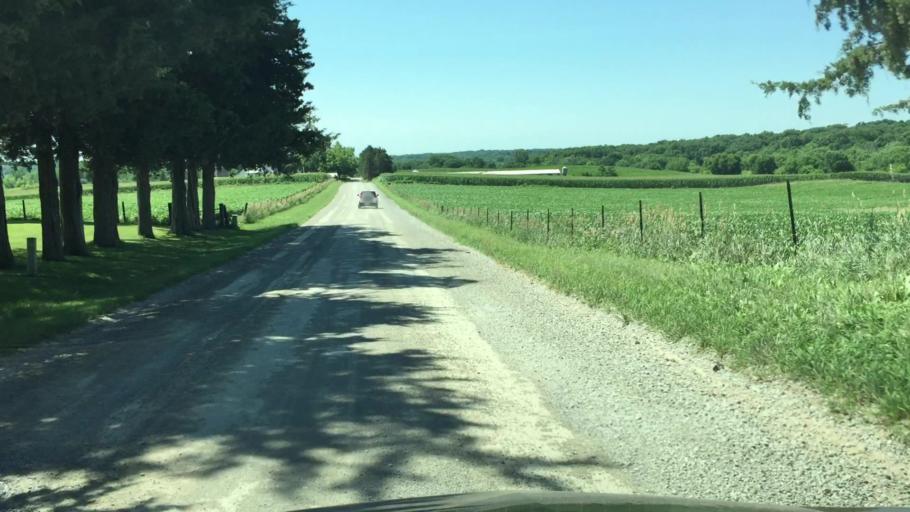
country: US
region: Iowa
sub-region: Linn County
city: Ely
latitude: 41.8277
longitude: -91.5899
